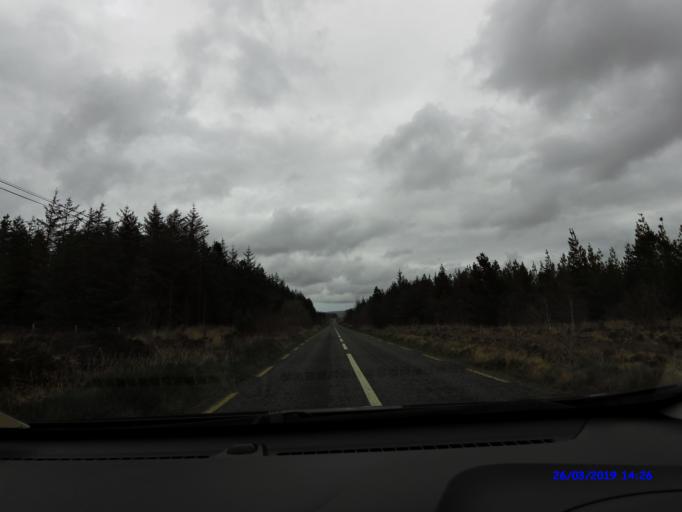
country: IE
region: Connaught
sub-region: Maigh Eo
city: Belmullet
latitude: 54.2452
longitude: -9.6412
